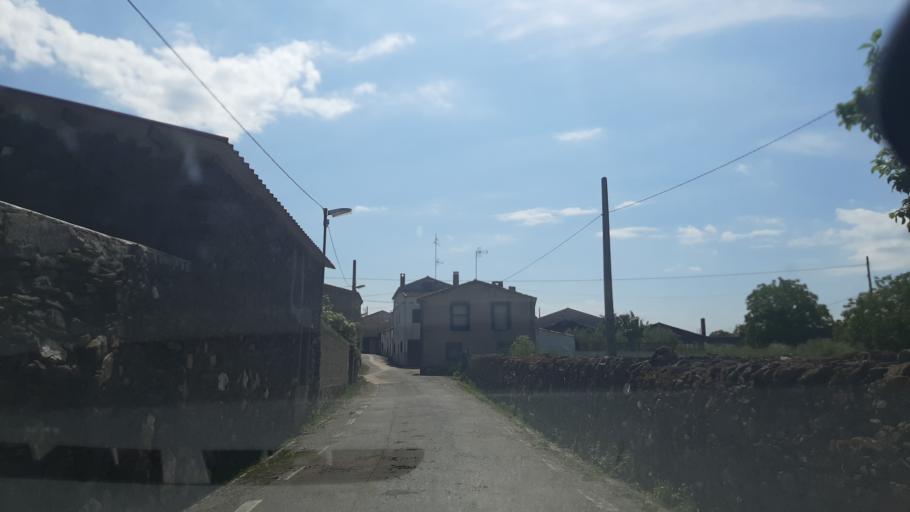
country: ES
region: Castille and Leon
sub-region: Provincia de Salamanca
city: Gallegos de Arganan
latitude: 40.6515
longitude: -6.7612
